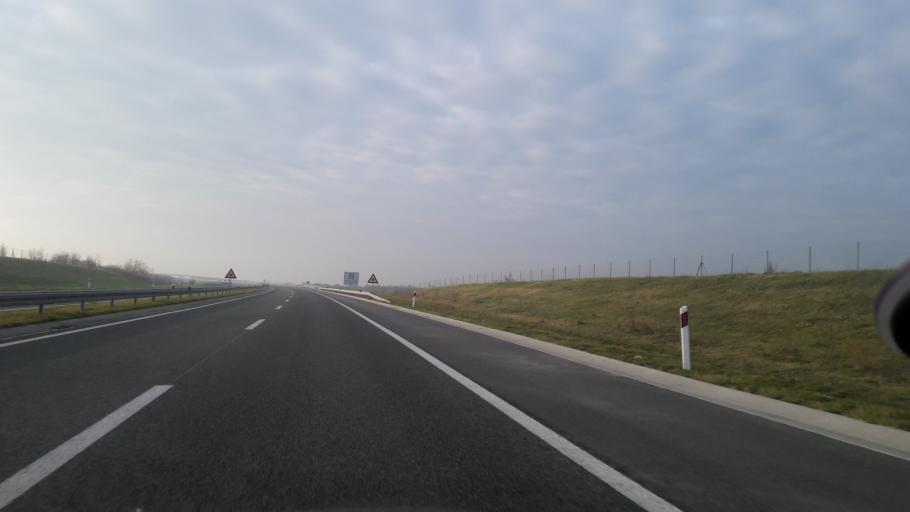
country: HR
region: Osjecko-Baranjska
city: Gorjani
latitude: 45.3897
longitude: 18.3995
